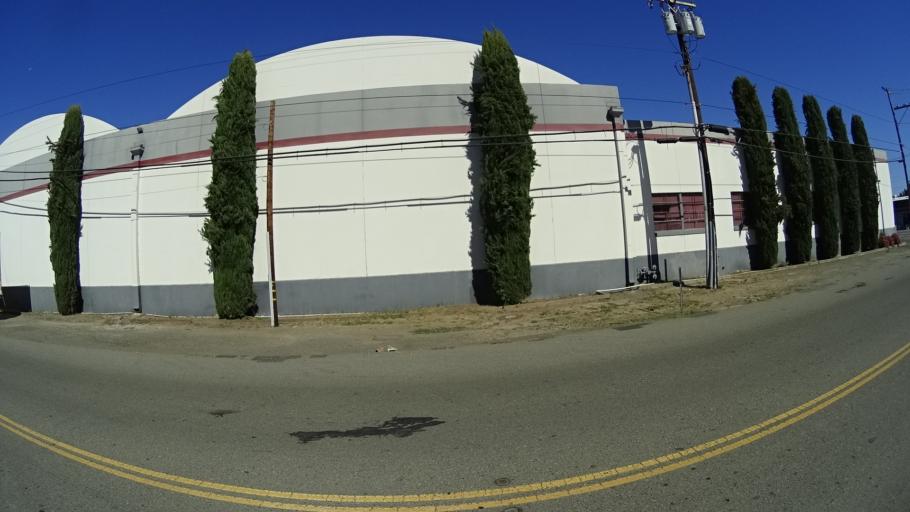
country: US
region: California
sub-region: Sacramento County
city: Sacramento
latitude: 38.5945
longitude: -121.4870
